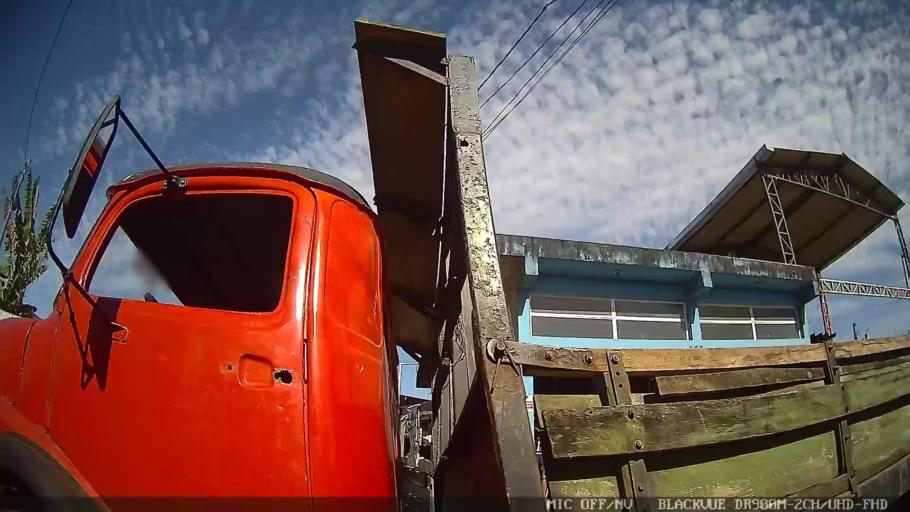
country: BR
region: Sao Paulo
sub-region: Guaruja
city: Guaruja
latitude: -23.9628
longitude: -46.2742
